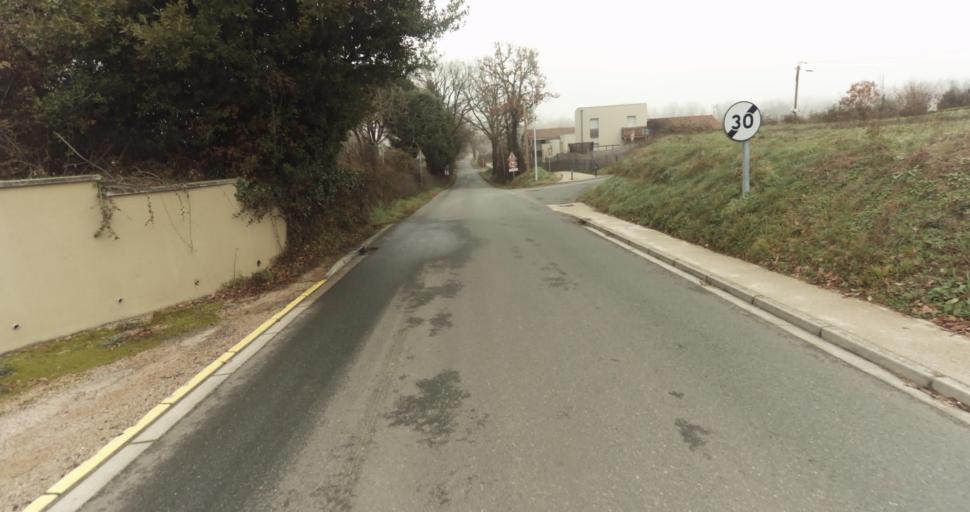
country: FR
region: Midi-Pyrenees
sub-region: Departement du Lot
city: Figeac
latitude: 44.6189
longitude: 2.0409
